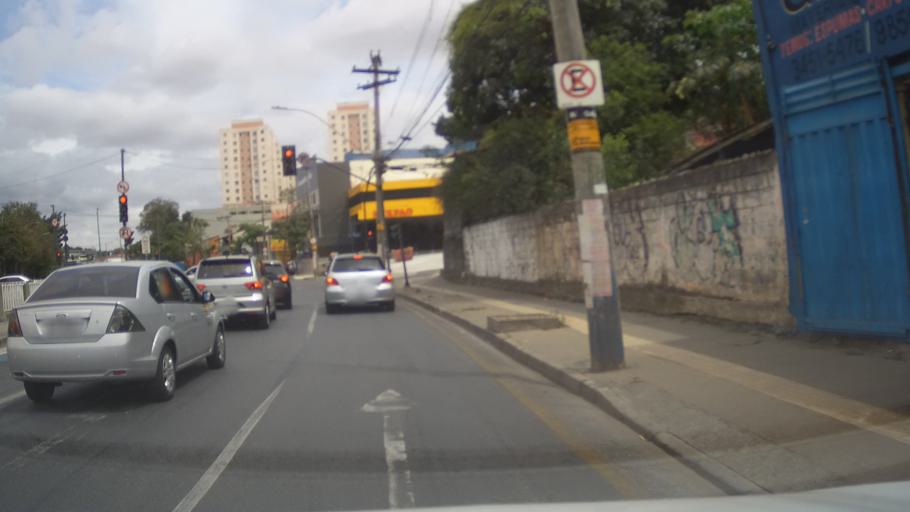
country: BR
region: Minas Gerais
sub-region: Belo Horizonte
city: Belo Horizonte
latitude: -19.8107
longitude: -43.9636
